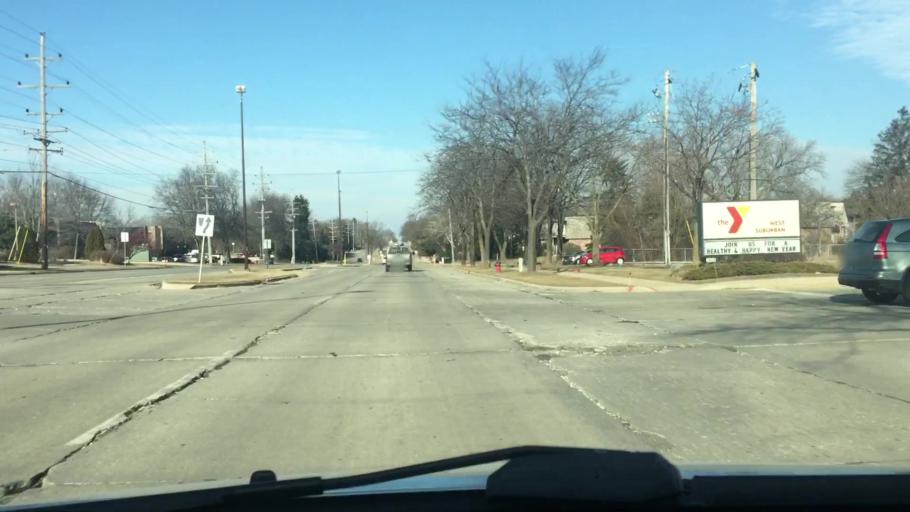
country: US
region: Wisconsin
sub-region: Waukesha County
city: Elm Grove
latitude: 43.0622
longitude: -88.0667
